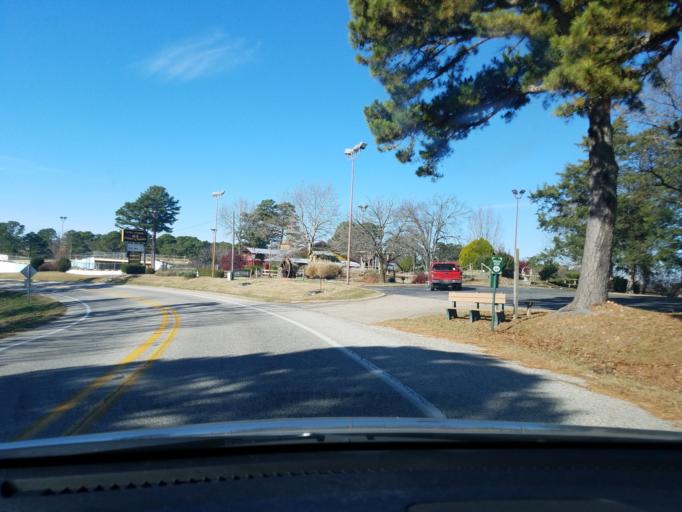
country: US
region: Arkansas
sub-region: Carroll County
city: Eureka Springs
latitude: 36.3902
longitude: -93.7147
